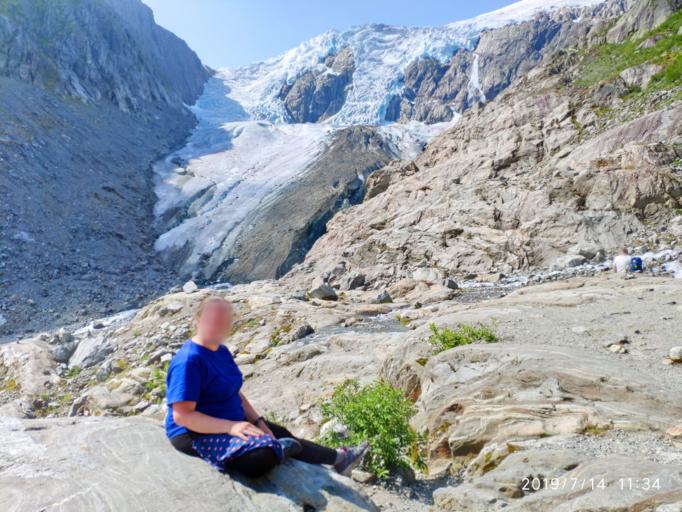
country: NO
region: Hordaland
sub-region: Odda
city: Odda
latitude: 60.0417
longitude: 6.4395
